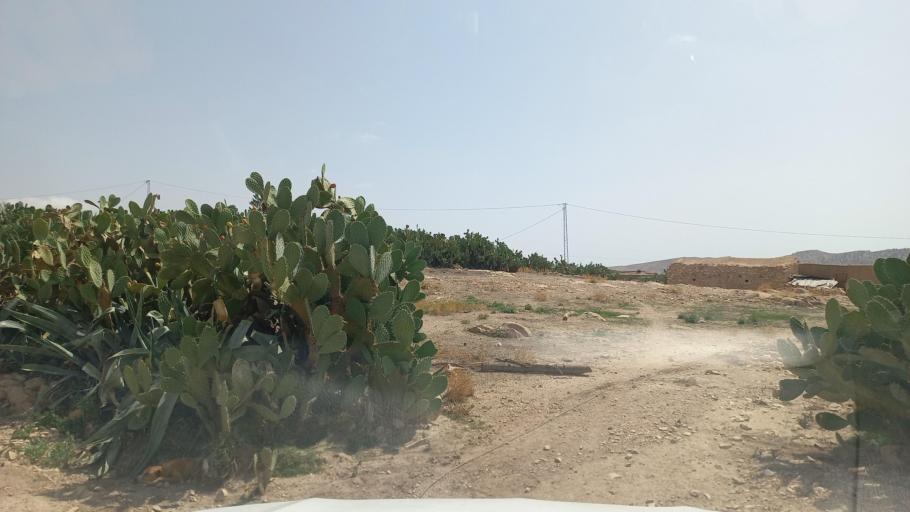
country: TN
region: Al Qasrayn
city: Sbiba
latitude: 35.4031
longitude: 8.9697
